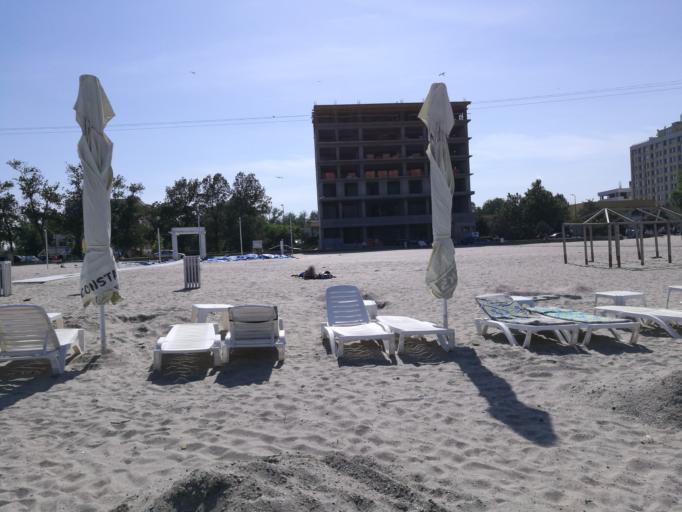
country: RO
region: Constanta
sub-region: Municipiul Constanta
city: Palazu Mare
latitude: 44.2282
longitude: 28.6300
